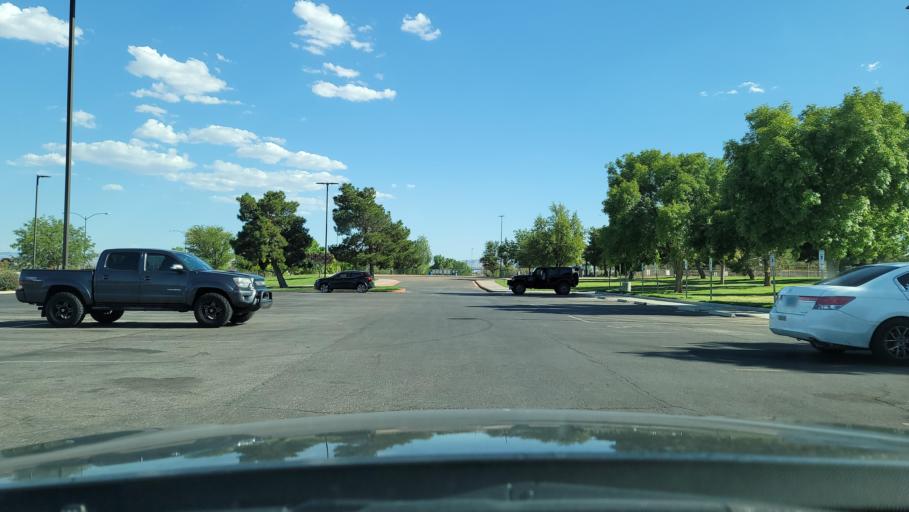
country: US
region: Nevada
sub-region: Clark County
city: Spring Valley
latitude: 36.1250
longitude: -115.2735
